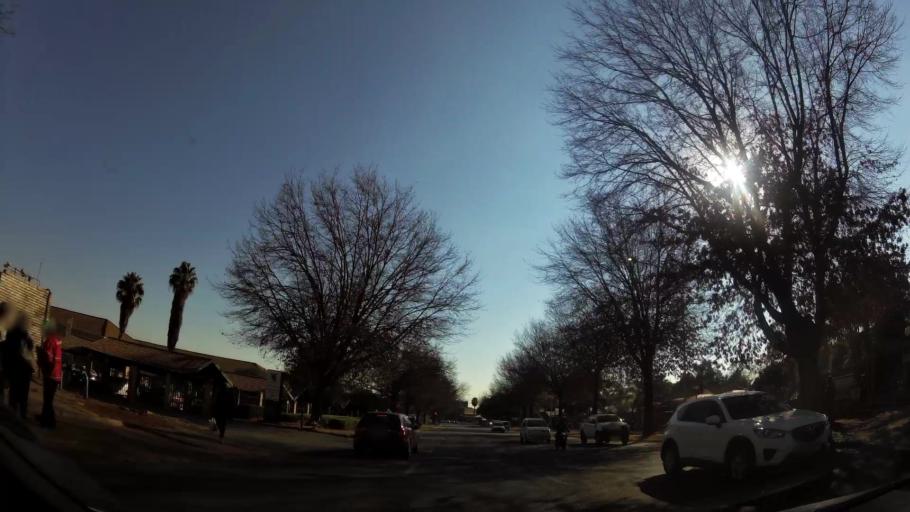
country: ZA
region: Gauteng
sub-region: Ekurhuleni Metropolitan Municipality
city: Germiston
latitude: -26.1817
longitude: 28.1362
